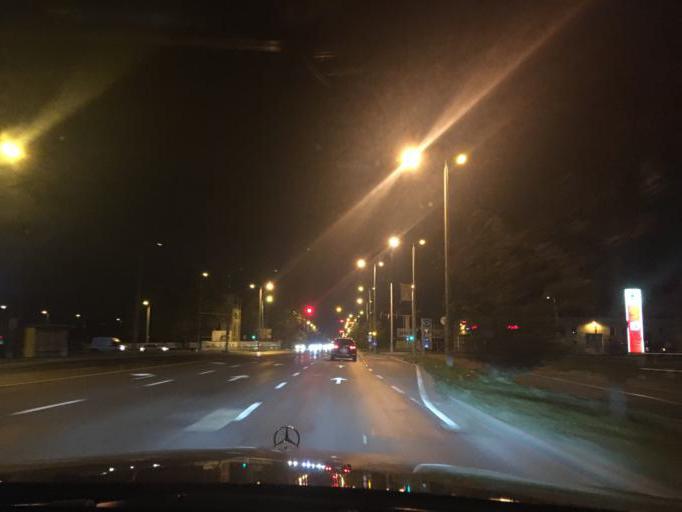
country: HU
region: Hajdu-Bihar
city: Debrecen
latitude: 47.5027
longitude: 21.6309
